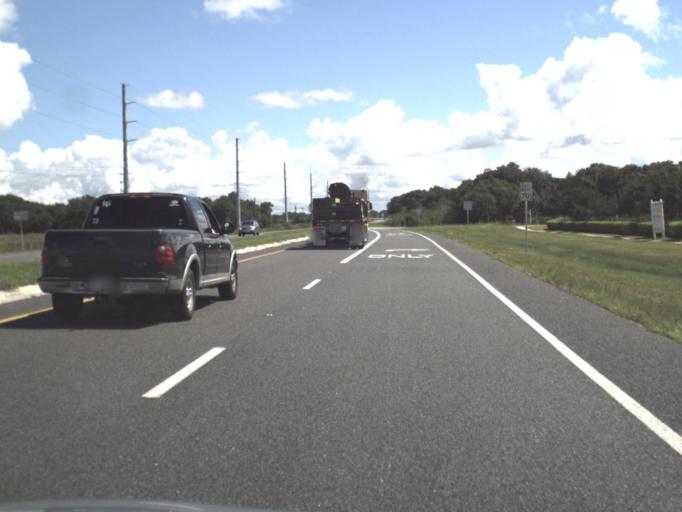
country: US
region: Florida
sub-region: Sarasota County
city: The Meadows
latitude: 27.4318
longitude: -82.3948
